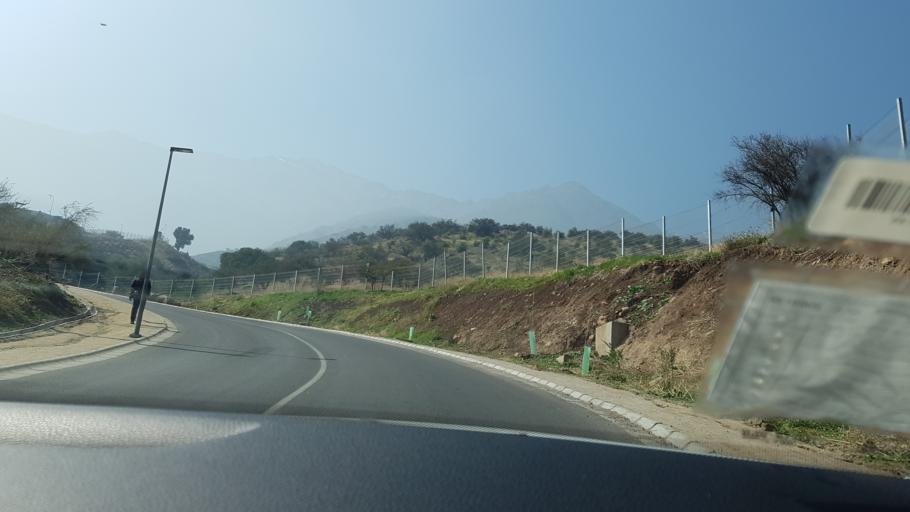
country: CL
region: Santiago Metropolitan
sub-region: Provincia de Santiago
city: Villa Presidente Frei, Nunoa, Santiago, Chile
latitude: -33.4814
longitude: -70.5183
